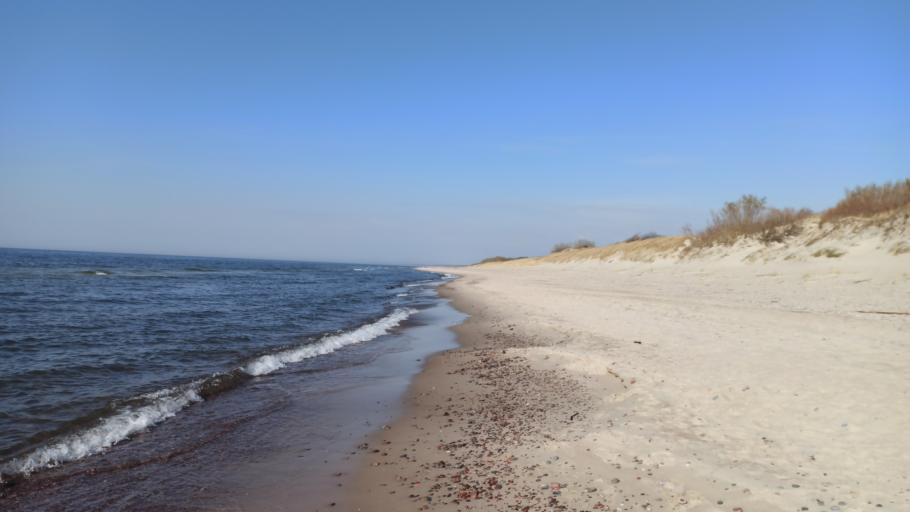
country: LT
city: Nida
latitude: 55.2261
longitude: 20.8924
